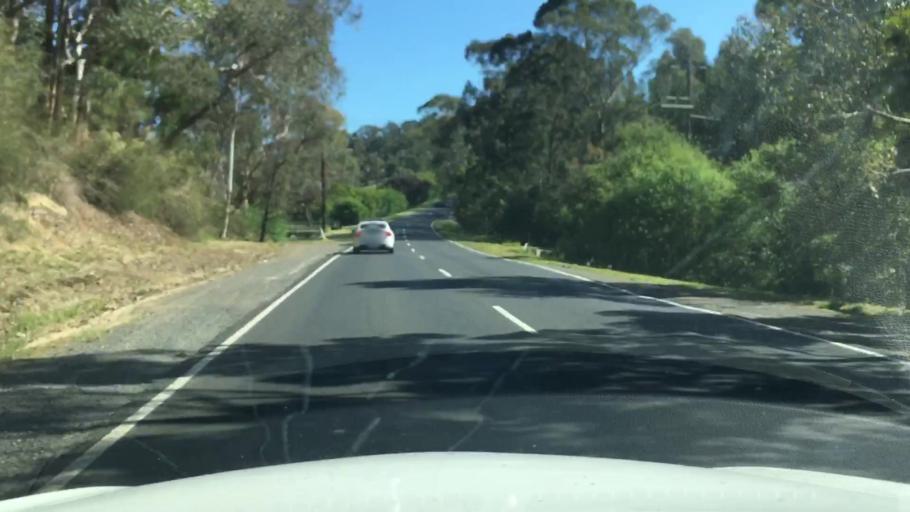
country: AU
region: Victoria
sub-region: Manningham
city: Park Orchards
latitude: -37.7578
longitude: 145.2059
